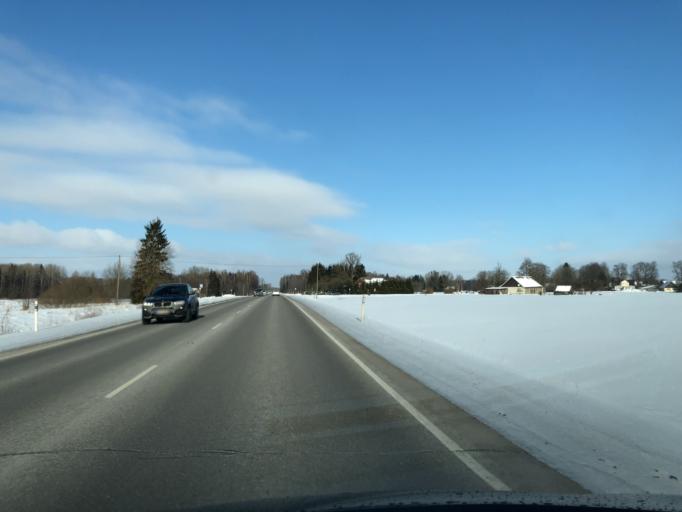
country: EE
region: Jaervamaa
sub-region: Paide linn
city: Paide
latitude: 58.8041
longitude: 25.7578
